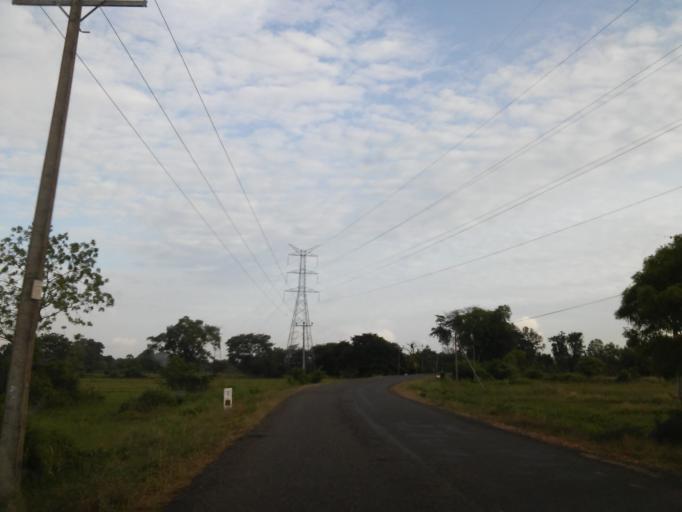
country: LK
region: Central
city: Sigiriya
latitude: 8.0970
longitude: 80.6333
